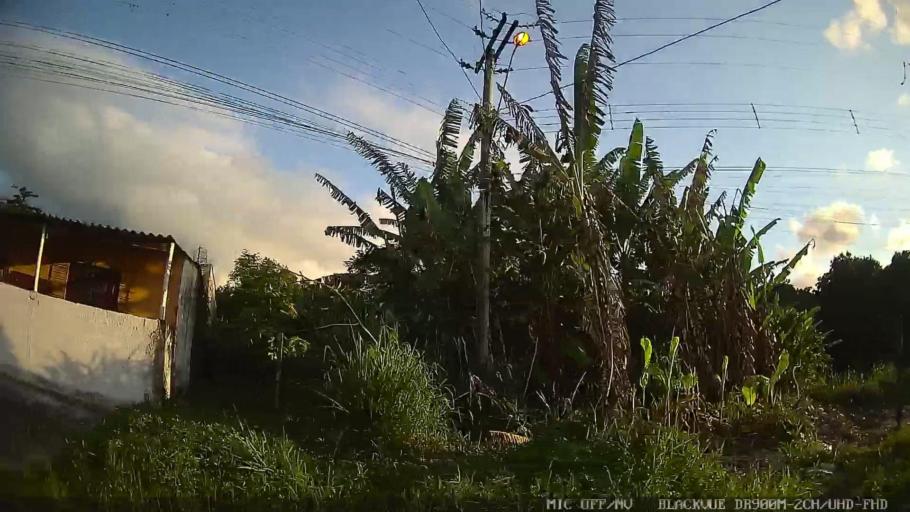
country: BR
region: Sao Paulo
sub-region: Itanhaem
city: Itanhaem
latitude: -24.1842
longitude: -46.8256
